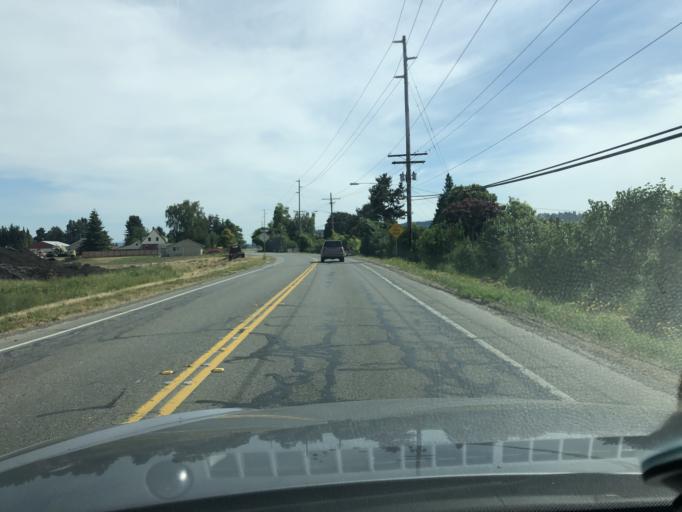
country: US
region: Washington
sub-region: King County
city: Kent
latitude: 47.3667
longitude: -122.2494
